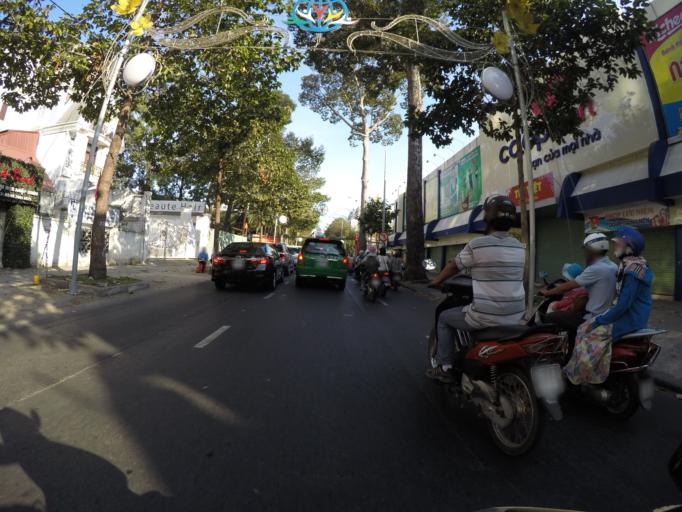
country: VN
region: Ho Chi Minh City
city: Quan Mot
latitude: 10.7817
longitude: 106.6925
